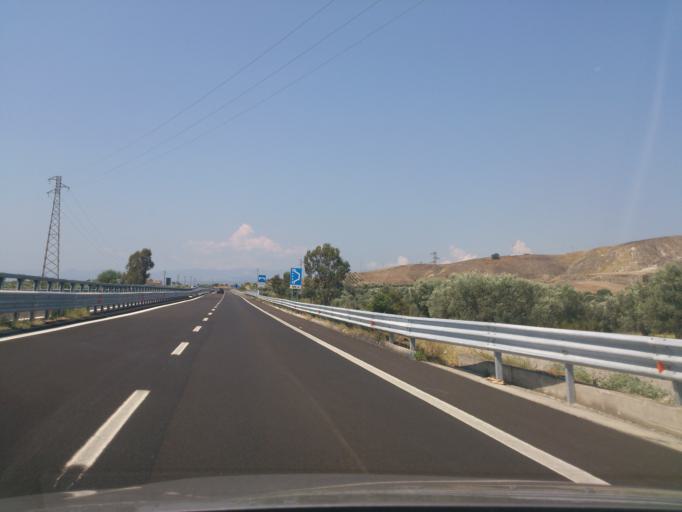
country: IT
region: Calabria
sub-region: Provincia di Reggio Calabria
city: Roccella Ionica
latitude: 38.3151
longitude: 16.3698
